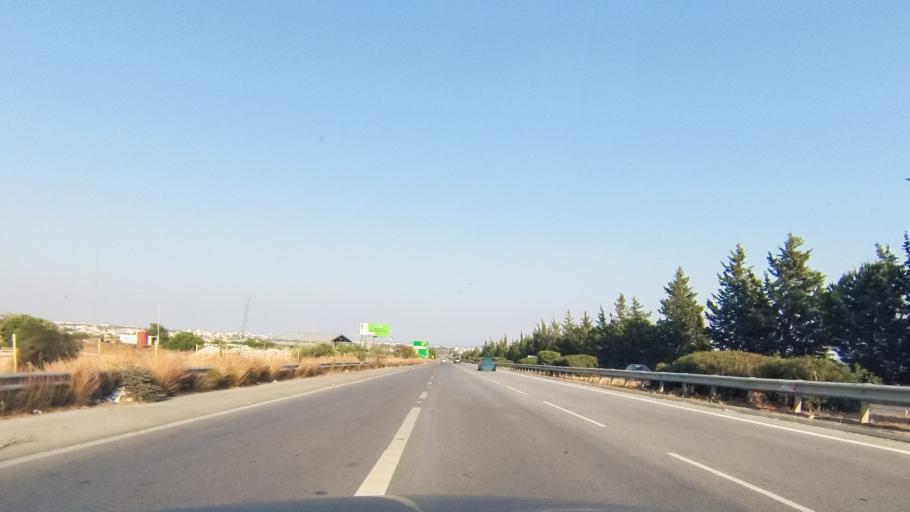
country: CY
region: Limassol
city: Ypsonas
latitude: 34.6938
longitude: 32.9709
